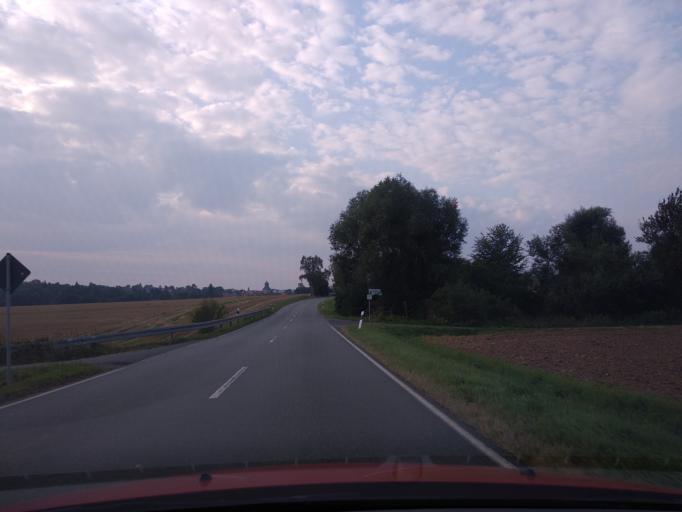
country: DE
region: Hesse
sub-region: Regierungsbezirk Kassel
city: Calden
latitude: 51.4117
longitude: 9.3490
